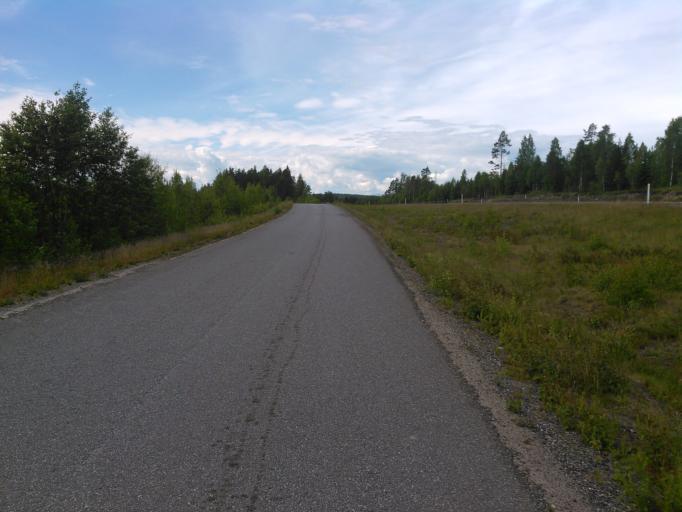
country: SE
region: Vaesterbotten
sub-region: Vannas Kommun
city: Vannasby
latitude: 63.8916
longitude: 19.9897
